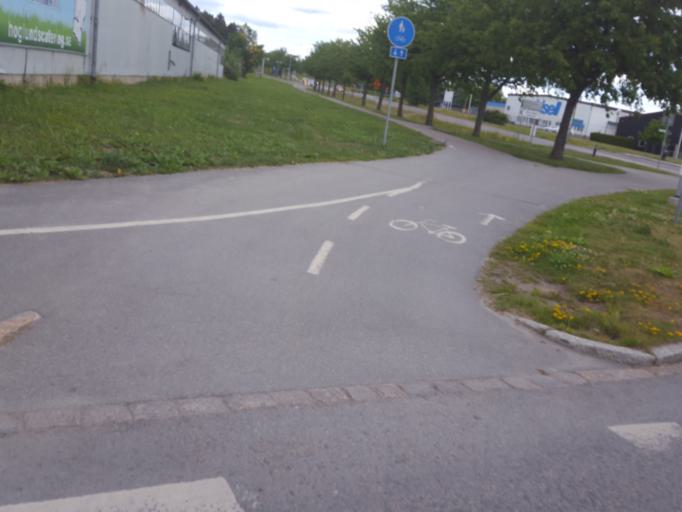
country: SE
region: Uppsala
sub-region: Uppsala Kommun
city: Saevja
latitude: 59.8476
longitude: 17.6782
